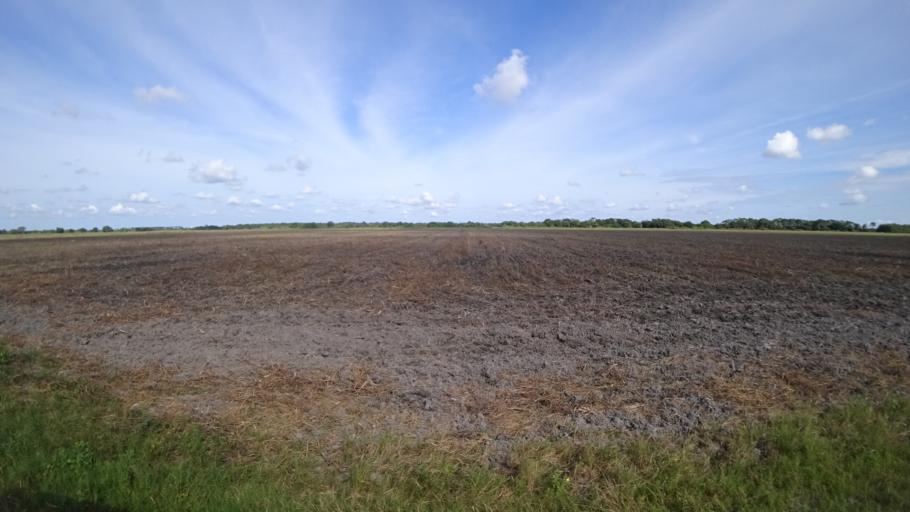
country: US
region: Florida
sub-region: Sarasota County
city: The Meadows
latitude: 27.4440
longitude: -82.3182
